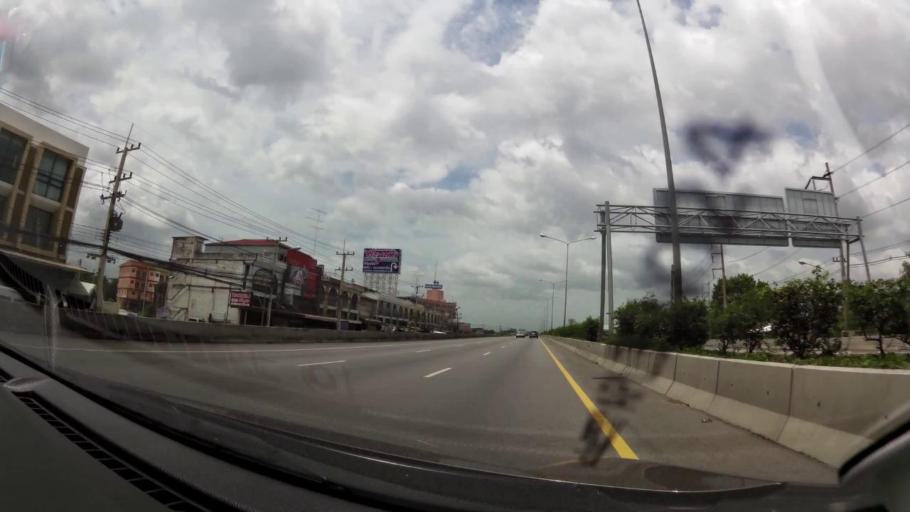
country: TH
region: Phetchaburi
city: Phetchaburi
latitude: 13.1047
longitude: 99.9344
